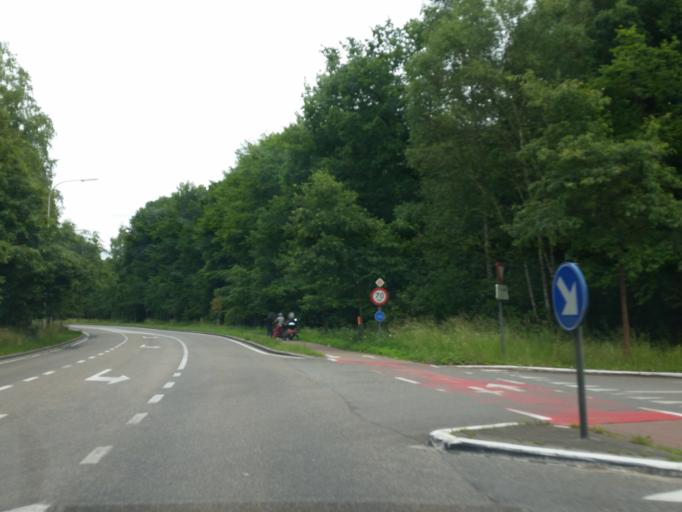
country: BE
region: Flanders
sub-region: Provincie Antwerpen
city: Brasschaat
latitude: 51.2852
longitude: 4.5041
